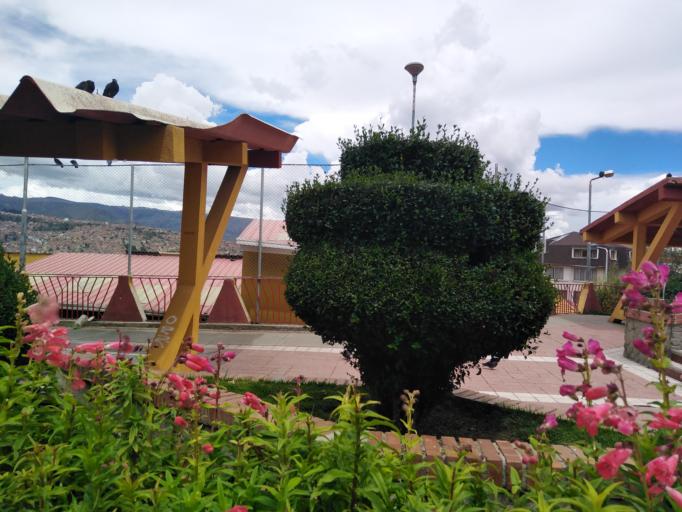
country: BO
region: La Paz
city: La Paz
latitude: -16.5107
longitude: -68.1358
